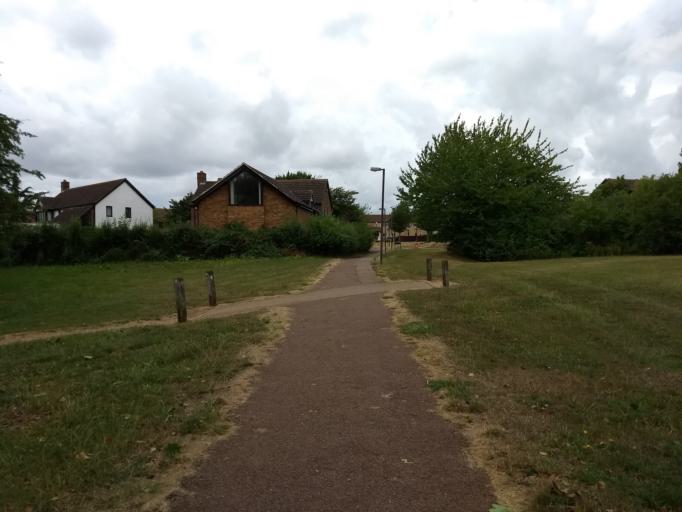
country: GB
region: England
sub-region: Milton Keynes
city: Bradwell
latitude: 52.0552
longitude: -0.7957
